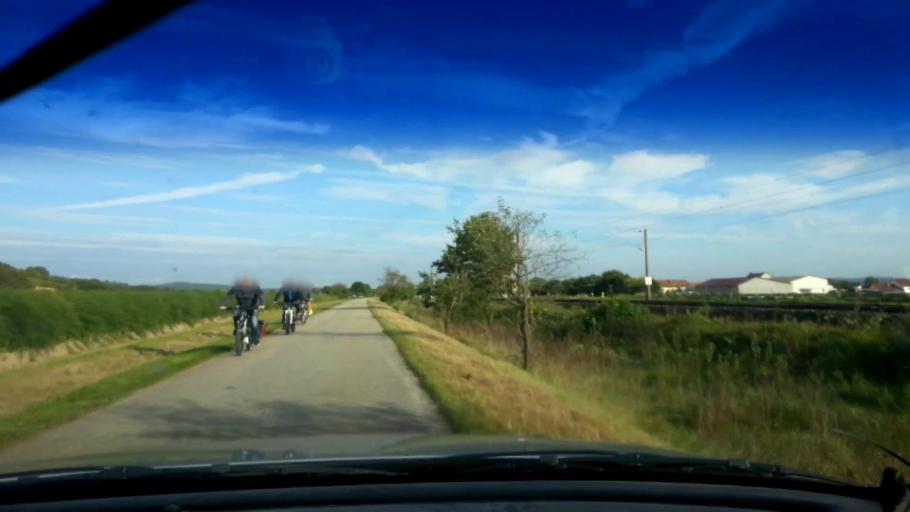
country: DE
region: Bavaria
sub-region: Upper Franconia
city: Viereth-Trunstadt
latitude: 49.9383
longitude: 10.7824
